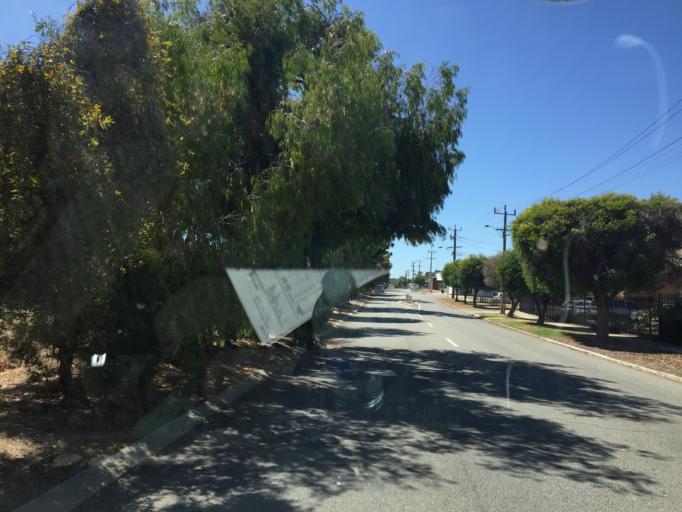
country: AU
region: Western Australia
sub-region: Victoria Park
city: Victoria Park
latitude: -31.9820
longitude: 115.9125
